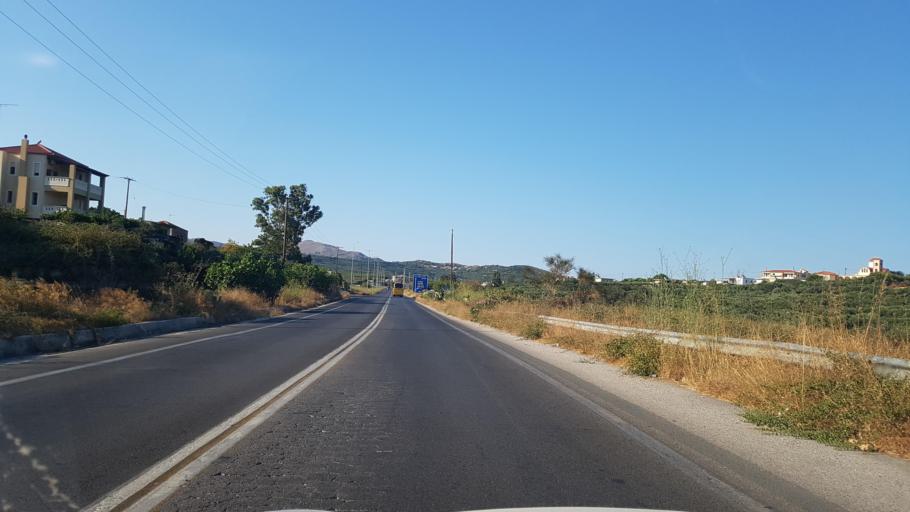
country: GR
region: Crete
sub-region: Nomos Chanias
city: Kolympari
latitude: 35.5224
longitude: 23.7468
